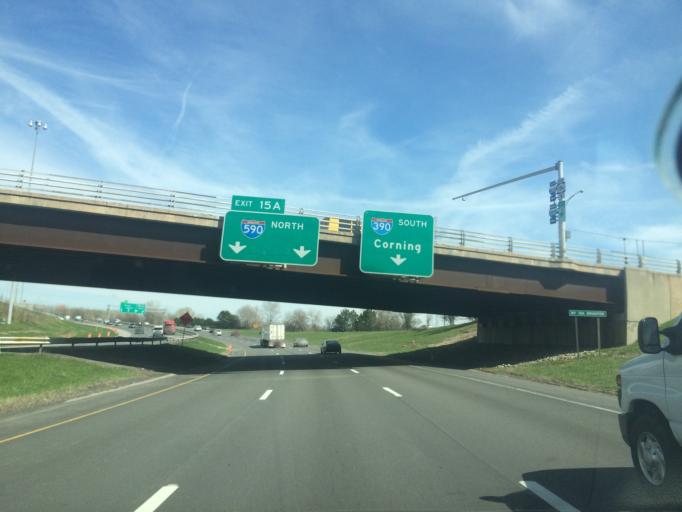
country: US
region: New York
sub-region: Monroe County
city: Rochester
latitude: 43.1080
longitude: -77.6168
